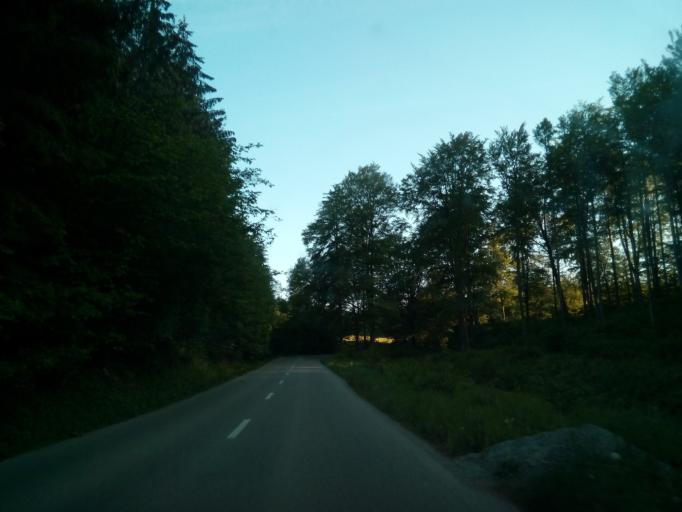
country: CZ
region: South Moravian
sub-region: Okres Blansko
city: Jedovnice
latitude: 49.2904
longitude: 16.7483
